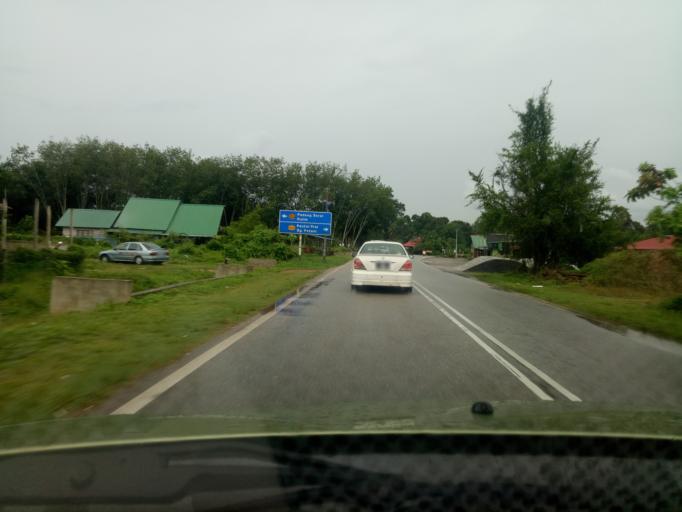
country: MY
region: Penang
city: Tasek Glugor
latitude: 5.5298
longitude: 100.5712
